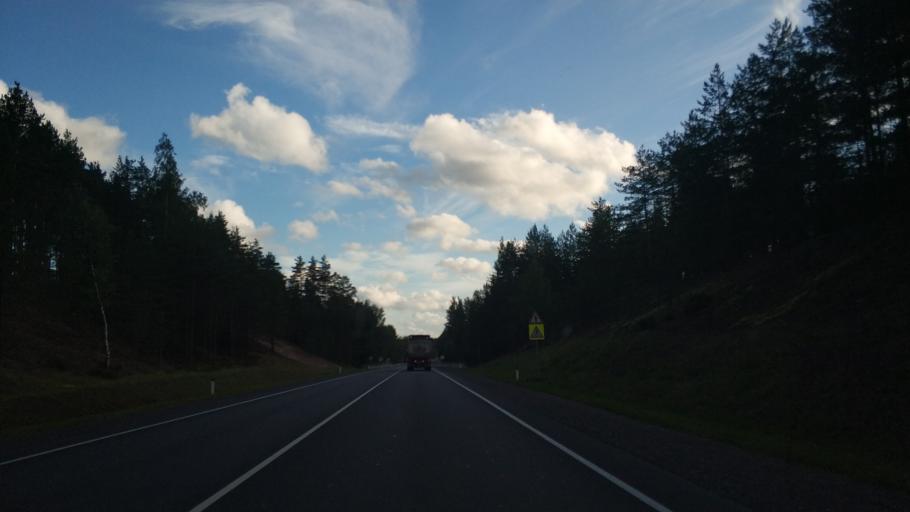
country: RU
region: Leningrad
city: Priozersk
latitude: 60.8682
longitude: 30.1603
